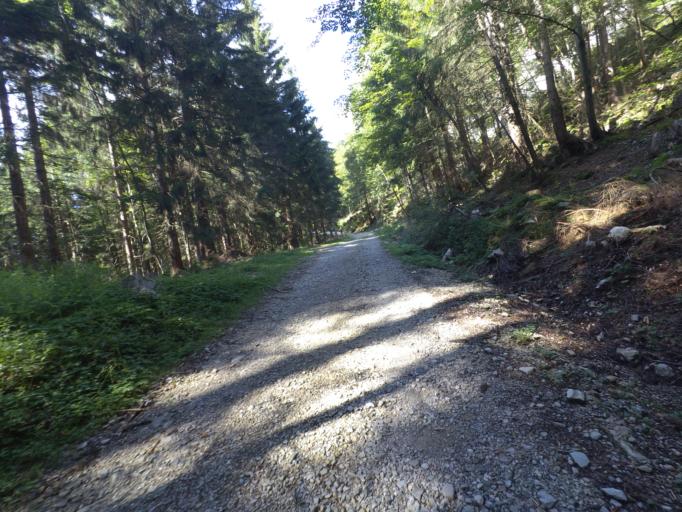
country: AT
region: Salzburg
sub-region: Politischer Bezirk Salzburg-Umgebung
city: Hintersee
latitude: 47.6971
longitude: 13.2446
